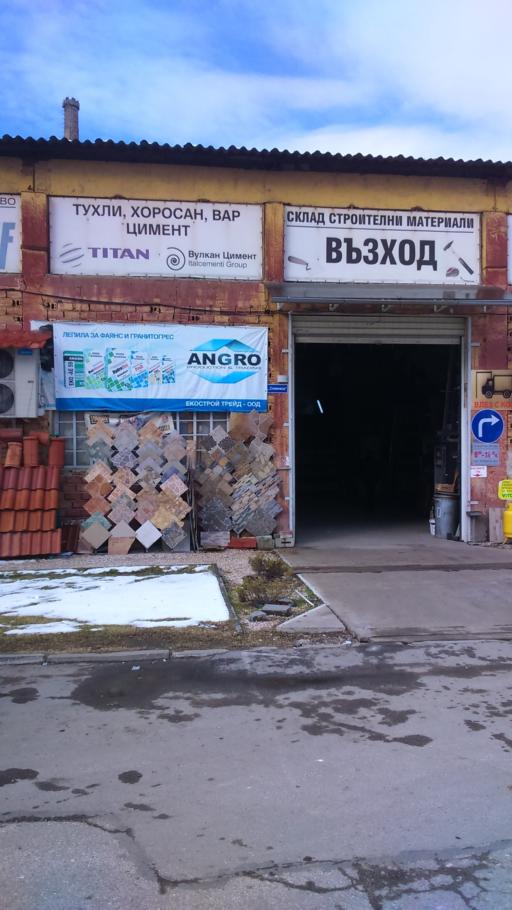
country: BG
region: Plovdiv
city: Stamboliyski
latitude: 42.1307
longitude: 24.5284
